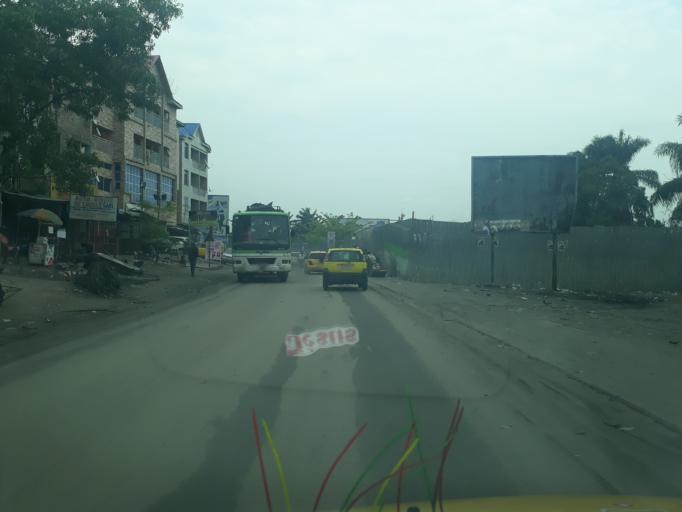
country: CD
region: Kinshasa
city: Kinshasa
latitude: -4.3416
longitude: 15.3040
